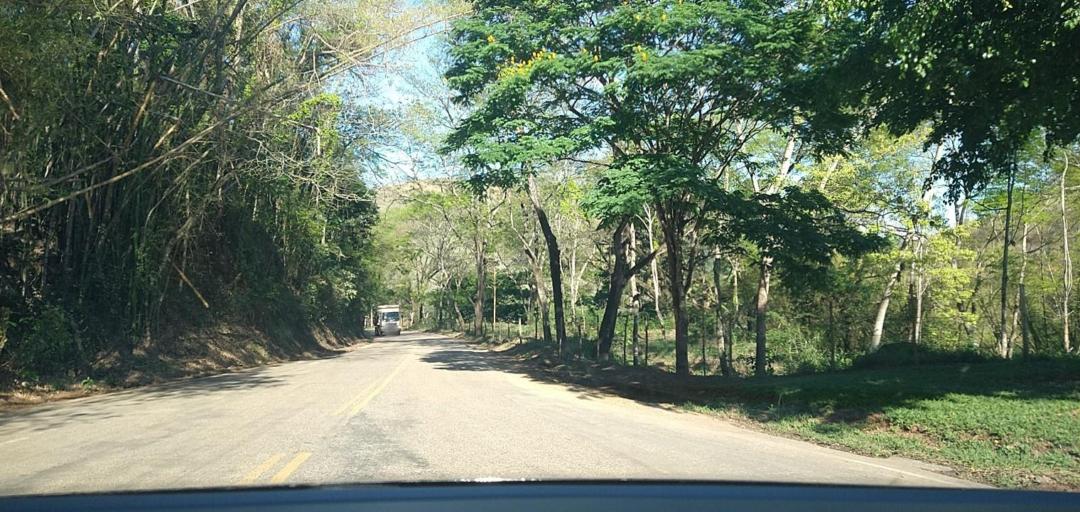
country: BR
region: Minas Gerais
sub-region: Ponte Nova
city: Ponte Nova
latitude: -20.2468
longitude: -42.8908
